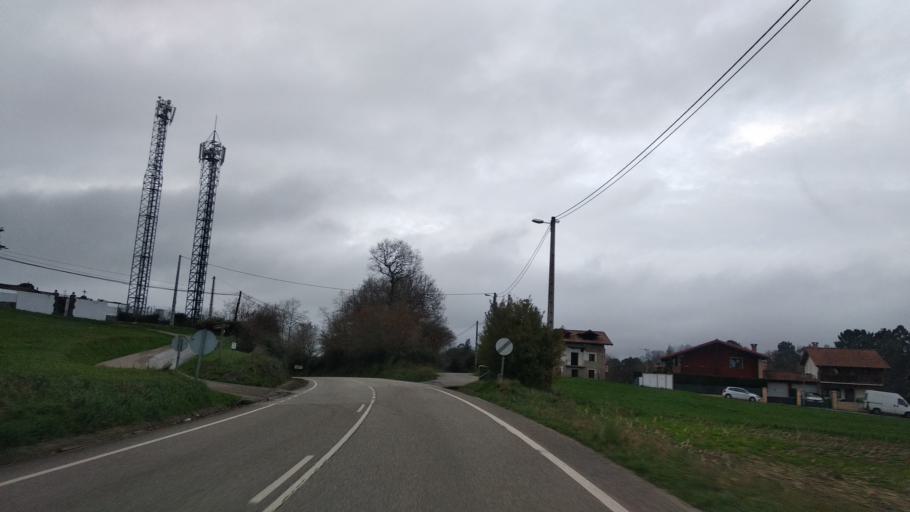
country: ES
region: Cantabria
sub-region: Provincia de Cantabria
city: Entrambasaguas
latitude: 43.4168
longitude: -3.7024
